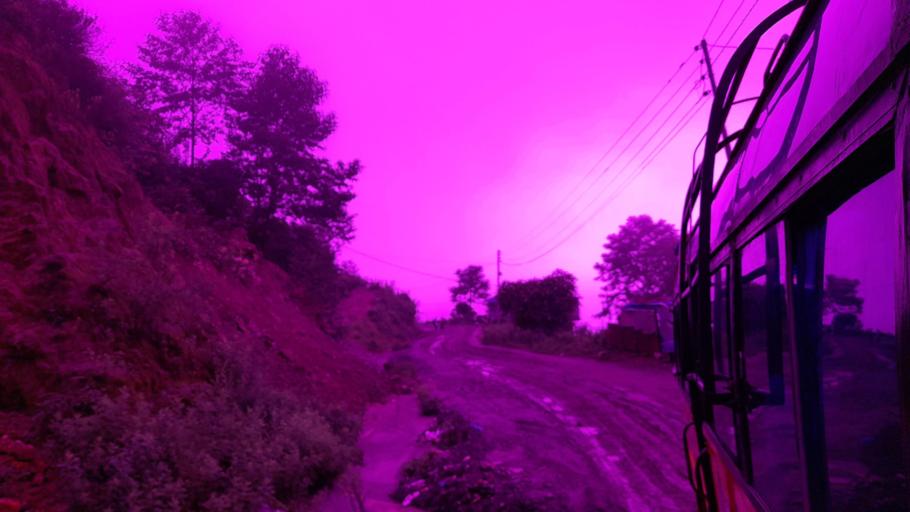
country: NP
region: Central Region
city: Kirtipur
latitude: 27.8209
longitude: 85.2250
